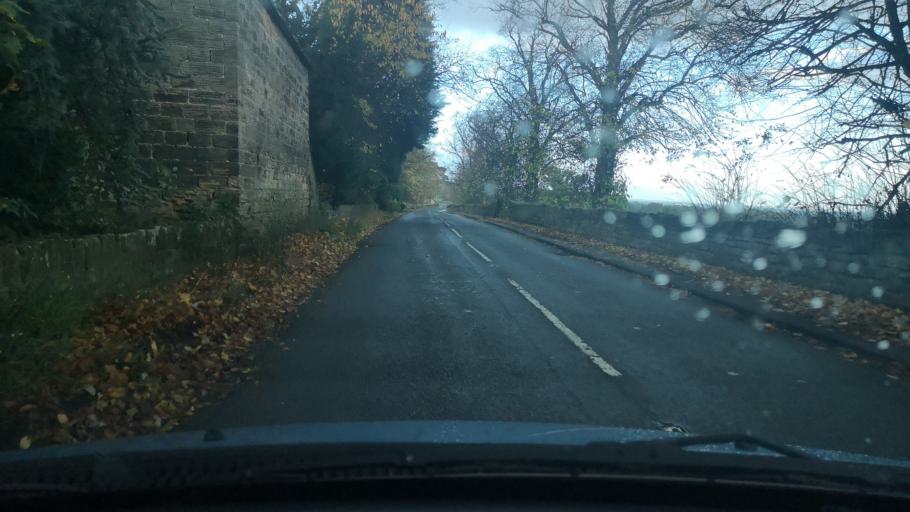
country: GB
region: England
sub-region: City and Borough of Wakefield
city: Woolley
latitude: 53.6157
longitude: -1.5170
